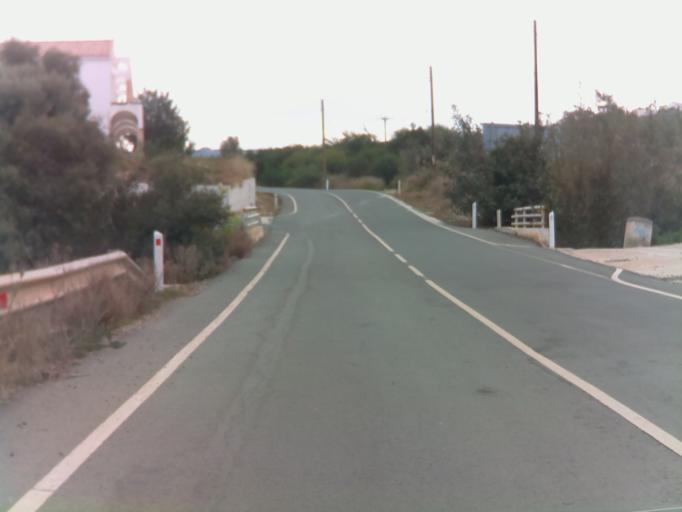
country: CY
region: Pafos
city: Polis
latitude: 35.0389
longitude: 32.3739
